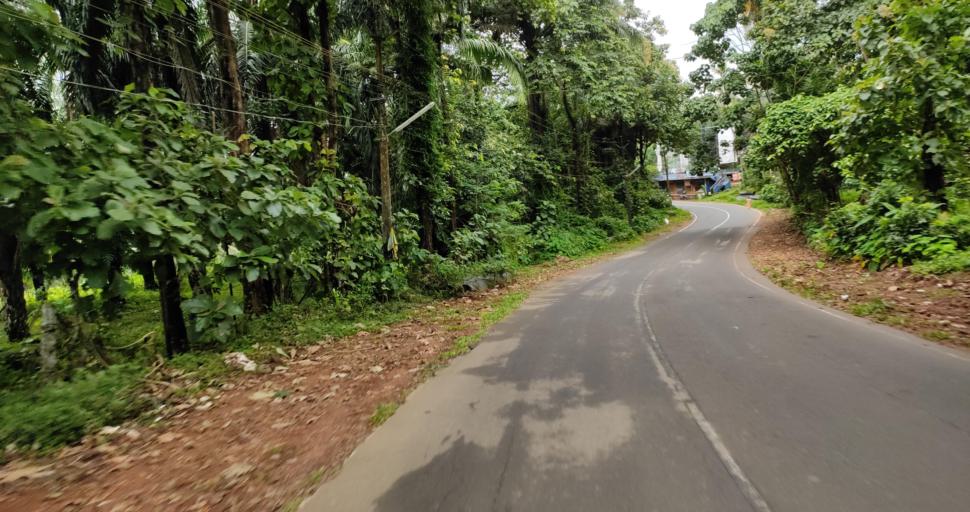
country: IN
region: Kerala
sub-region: Ernakulam
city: Angamali
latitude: 10.2932
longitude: 76.4956
